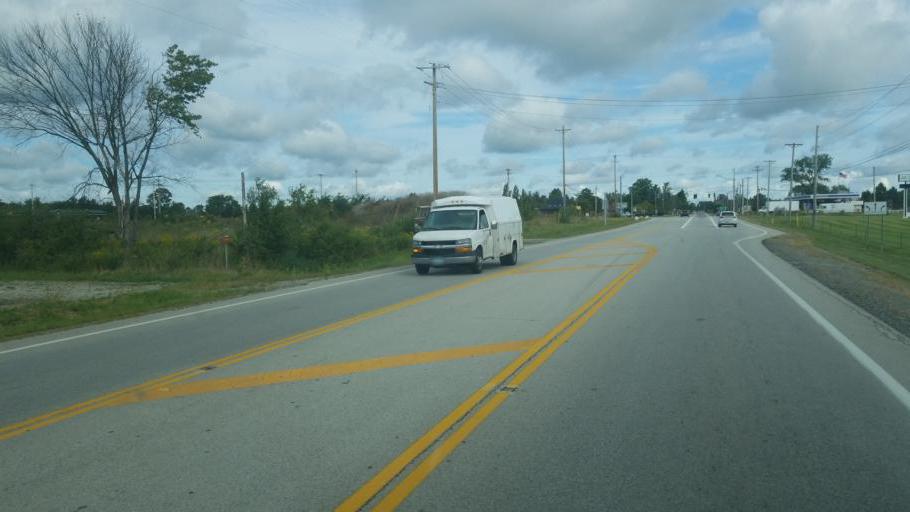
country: US
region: Ohio
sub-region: Lorain County
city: Oberlin
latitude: 41.2636
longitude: -82.2174
